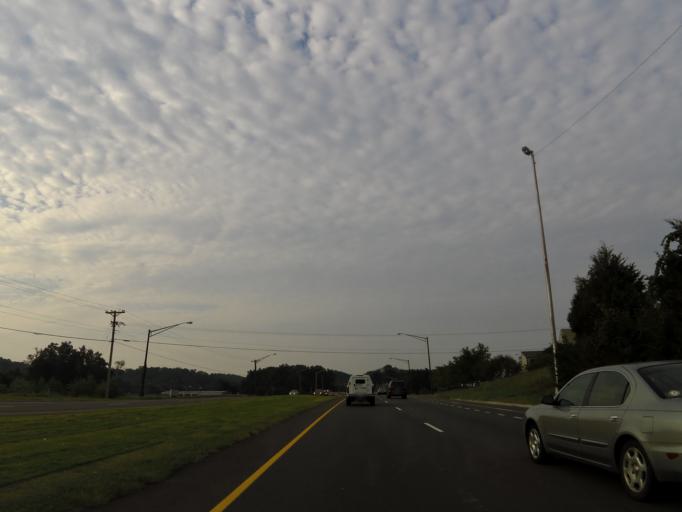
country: US
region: Tennessee
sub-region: Knox County
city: Knoxville
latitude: 35.9037
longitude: -83.9539
